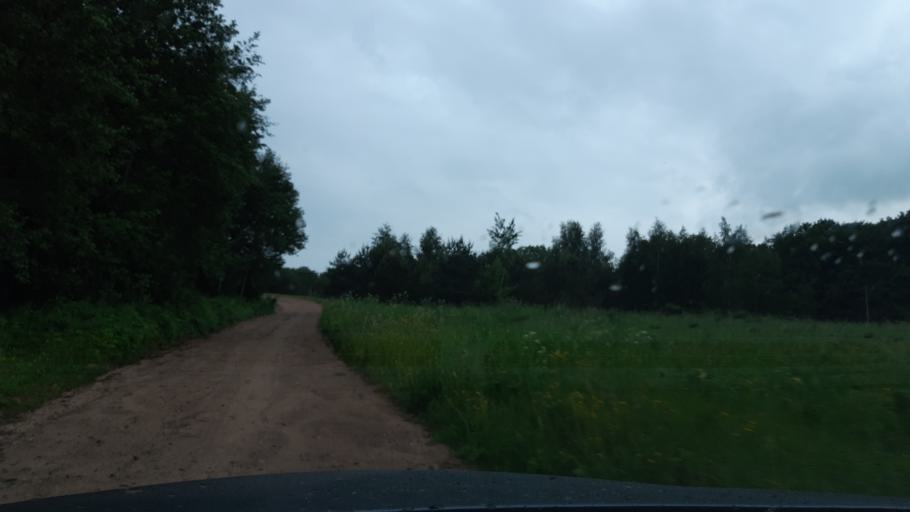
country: LT
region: Utenos apskritis
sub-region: Anyksciai
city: Anyksciai
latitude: 55.4525
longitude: 25.2140
